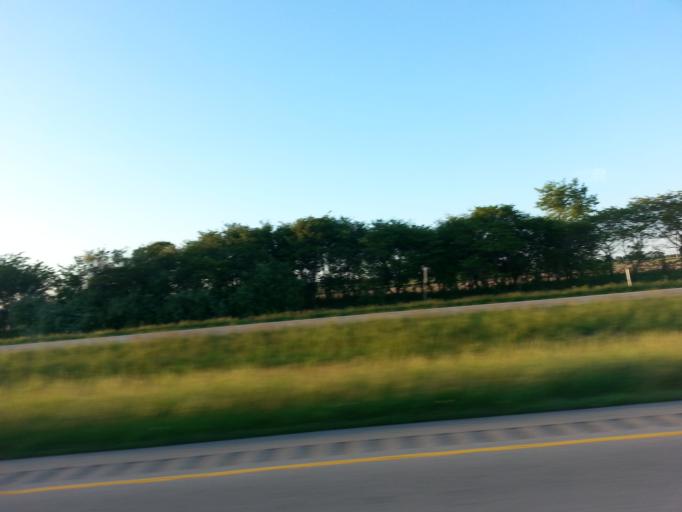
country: US
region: Indiana
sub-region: Fountain County
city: Veedersburg
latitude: 40.1265
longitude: -87.3077
